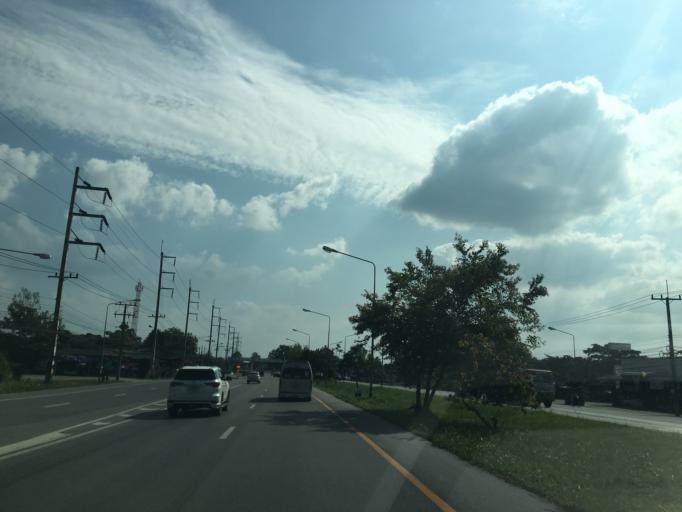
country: TH
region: Chiang Rai
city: Mae Lao
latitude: 19.7228
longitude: 99.7161
